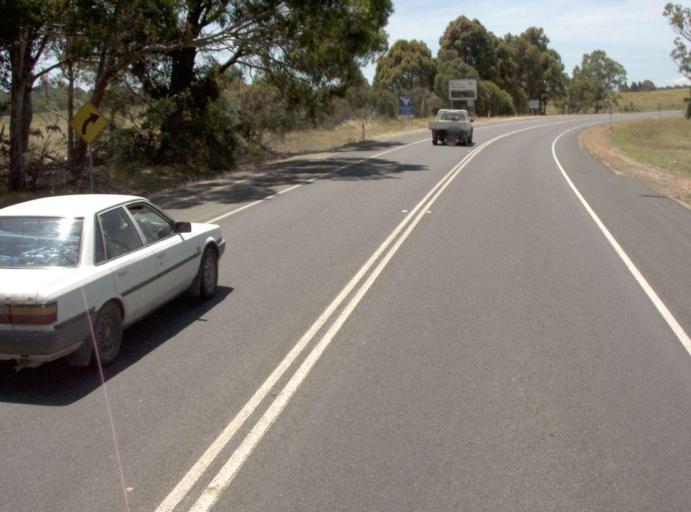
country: AU
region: Victoria
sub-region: East Gippsland
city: Bairnsdale
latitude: -37.8075
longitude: 147.6491
